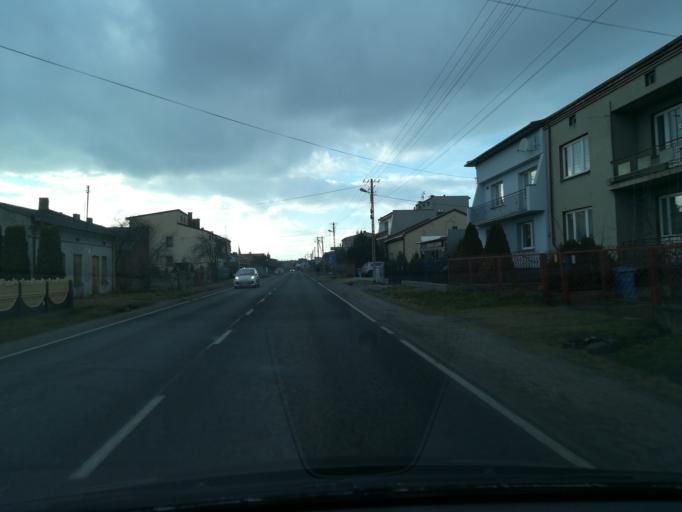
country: PL
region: Lodz Voivodeship
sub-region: Powiat radomszczanski
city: Radomsko
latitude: 51.0762
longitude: 19.4021
